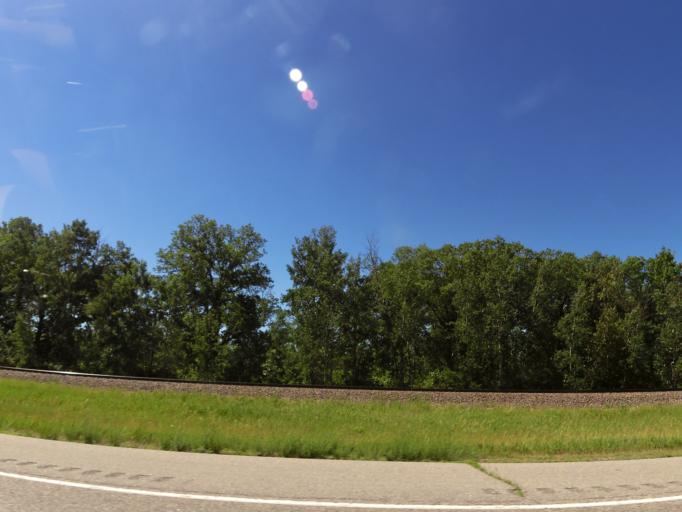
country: US
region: Minnesota
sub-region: Red Lake County
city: Red Lake Falls
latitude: 47.6938
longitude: -96.1067
